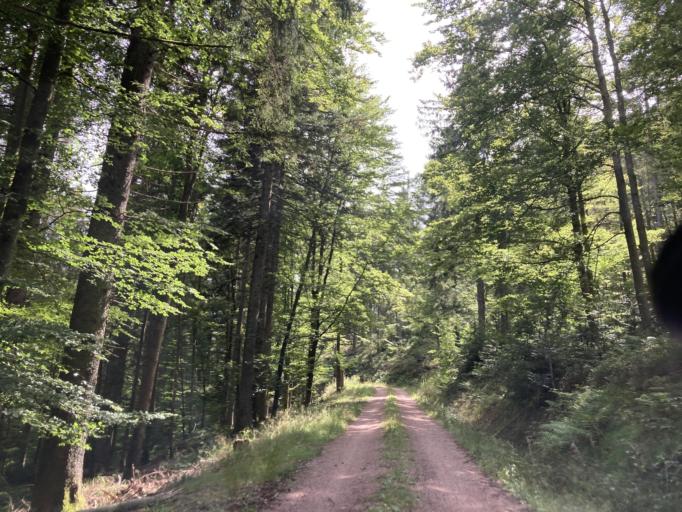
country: DE
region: Baden-Wuerttemberg
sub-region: Freiburg Region
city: Schonach im Schwarzwald
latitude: 48.1635
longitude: 8.1383
